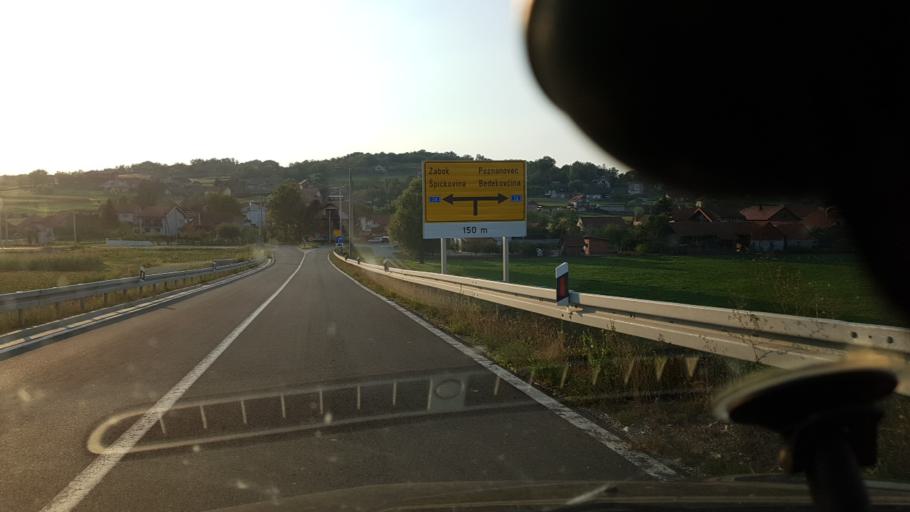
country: HR
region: Krapinsko-Zagorska
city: Bedekovcina
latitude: 46.0377
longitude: 15.9827
